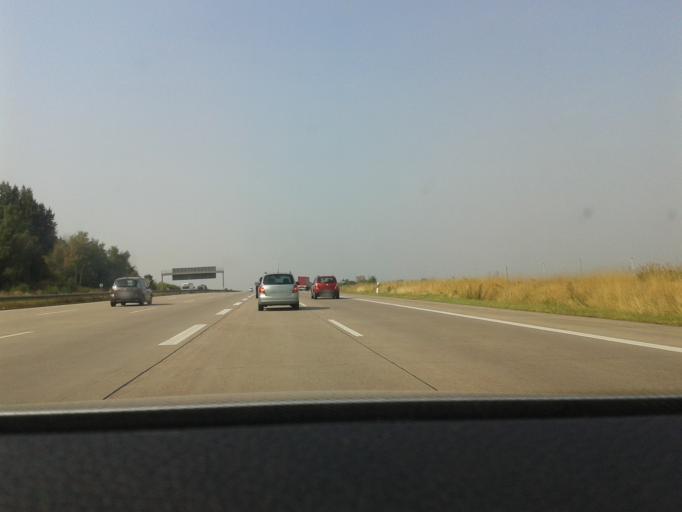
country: DE
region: Saxony
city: Reinsberg
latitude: 51.0559
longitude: 13.3712
